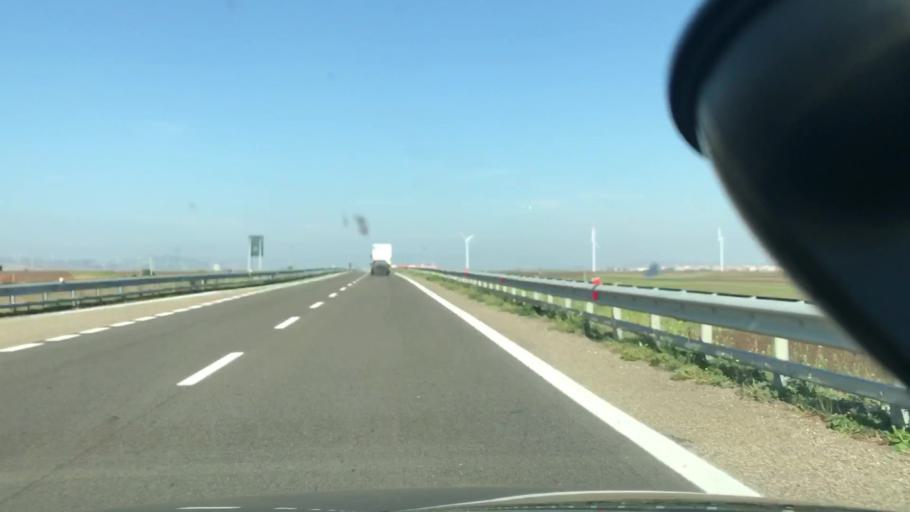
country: IT
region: Basilicate
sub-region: Provincia di Potenza
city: Lavello
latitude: 41.0149
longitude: 15.8237
